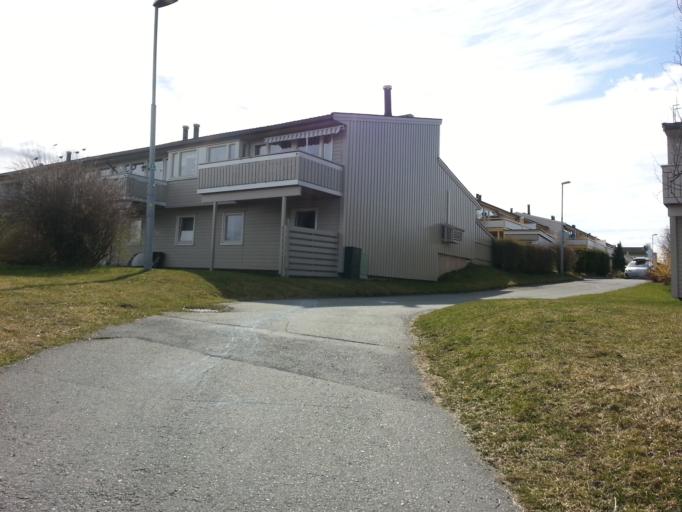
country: NO
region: Sor-Trondelag
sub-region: Trondheim
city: Trondheim
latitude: 63.4276
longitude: 10.4493
